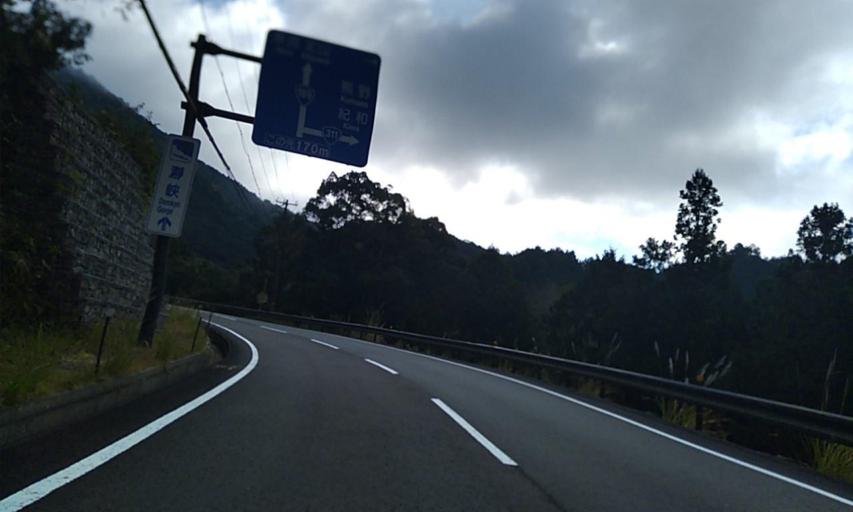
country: JP
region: Wakayama
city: Shingu
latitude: 33.8769
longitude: 135.8739
